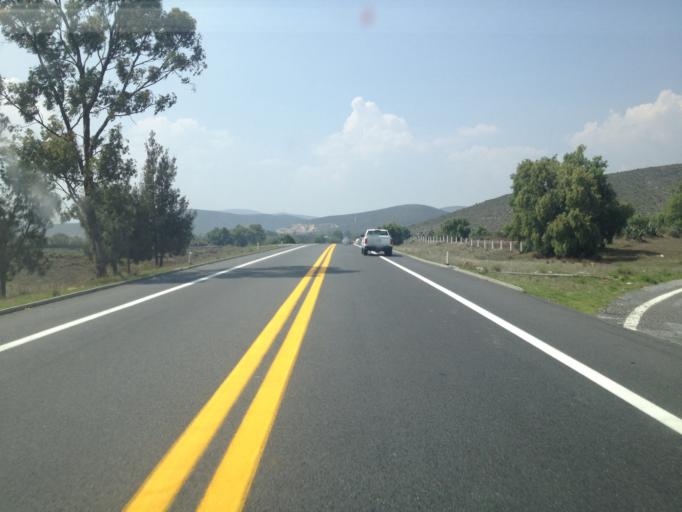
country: MX
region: Puebla
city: Cuacnopalan
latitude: 18.8143
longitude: -97.4909
